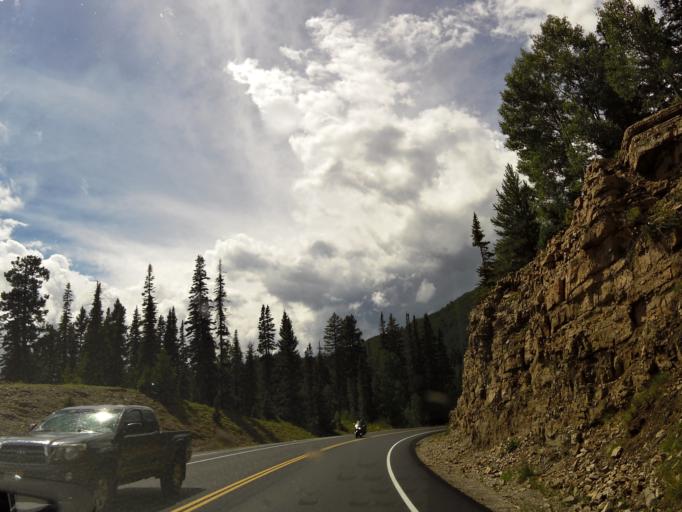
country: US
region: Colorado
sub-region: San Juan County
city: Silverton
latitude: 37.6791
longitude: -107.7925
